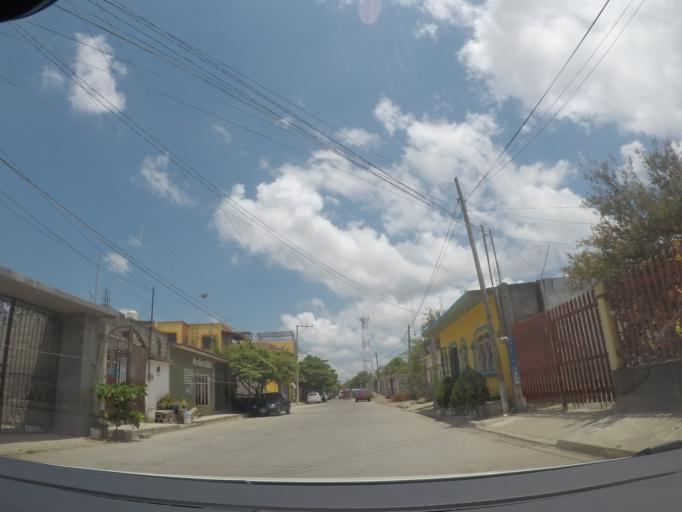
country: MX
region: Oaxaca
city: Juchitan de Zaragoza
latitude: 16.4402
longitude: -95.0132
